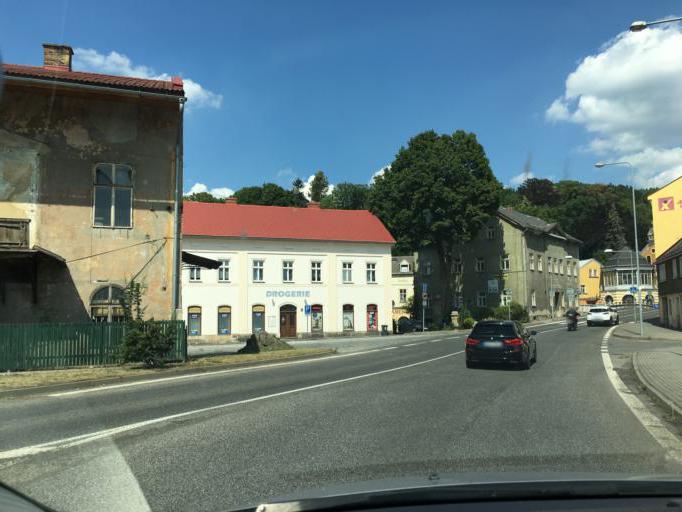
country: CZ
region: Ustecky
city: Ceska Kamenice
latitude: 50.7996
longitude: 14.4209
